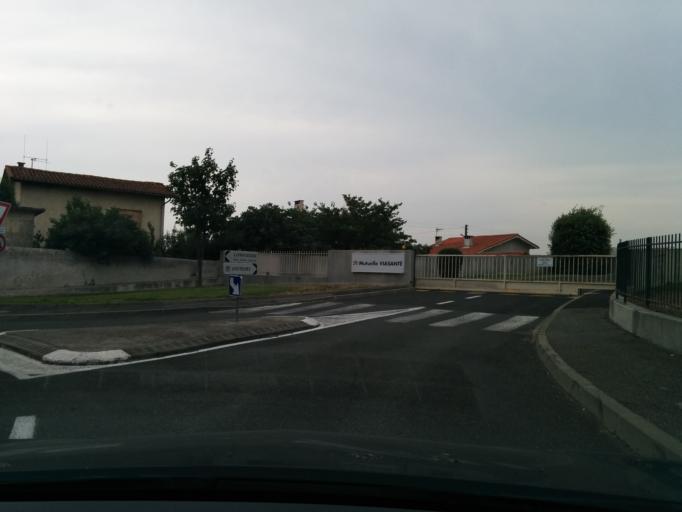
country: FR
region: Languedoc-Roussillon
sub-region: Departement de l'Aude
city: Carcassonne
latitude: 43.2224
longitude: 2.3375
